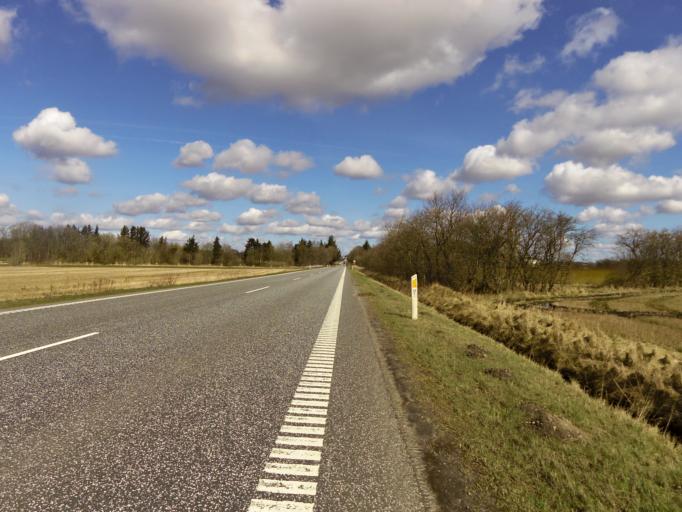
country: DK
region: South Denmark
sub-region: Tonder Kommune
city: Toftlund
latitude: 55.1702
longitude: 9.0527
